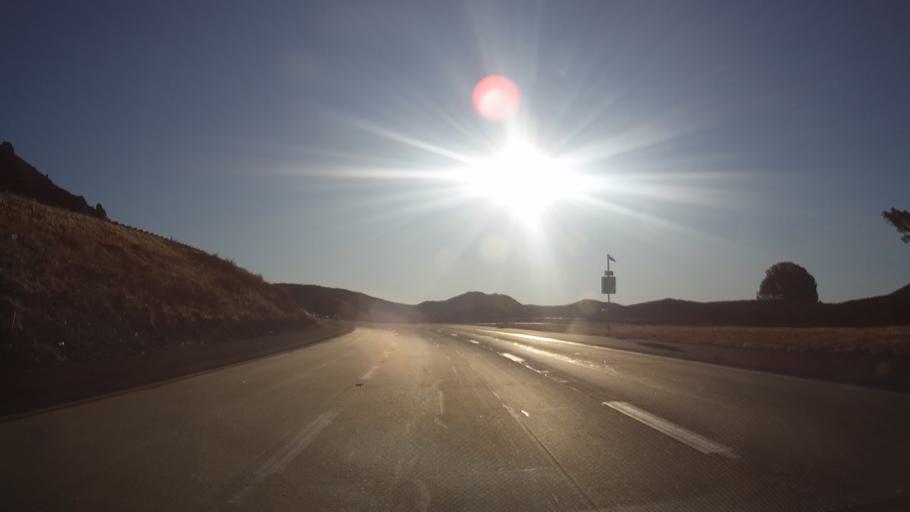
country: US
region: California
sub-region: San Diego County
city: Descanso
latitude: 32.8373
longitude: -116.6605
